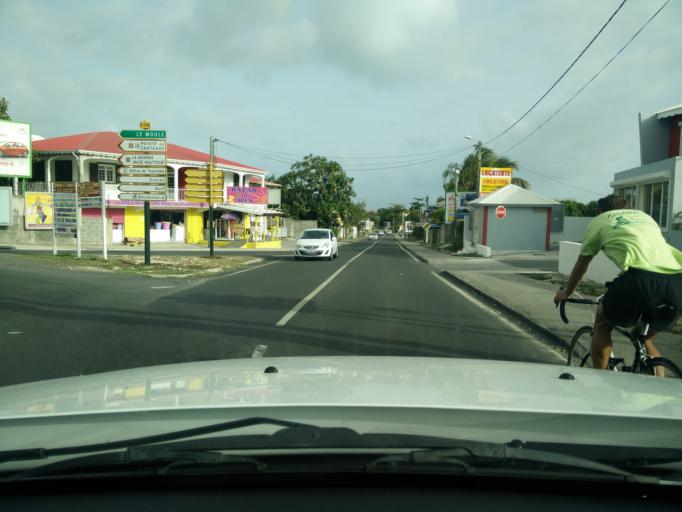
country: GP
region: Guadeloupe
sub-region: Guadeloupe
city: Saint-Francois
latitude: 16.2561
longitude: -61.2898
